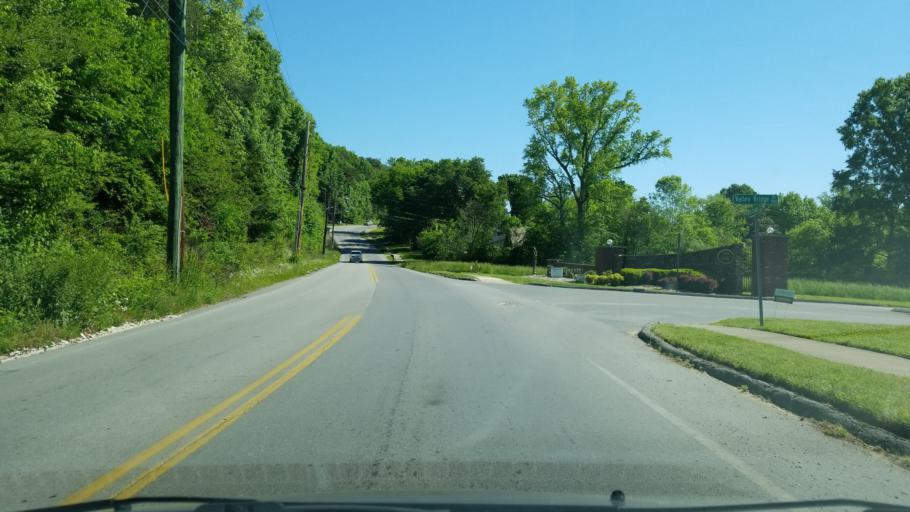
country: US
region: Tennessee
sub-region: Hamilton County
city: Red Bank
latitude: 35.1196
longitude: -85.3158
